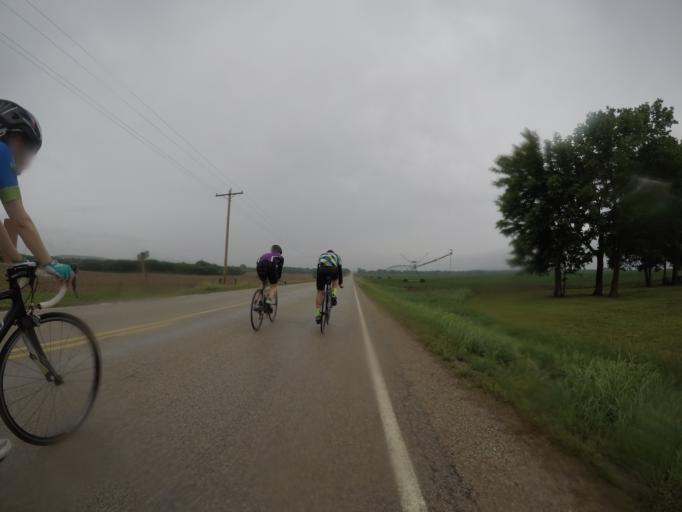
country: US
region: Kansas
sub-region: Pottawatomie County
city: Wamego
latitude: 39.3468
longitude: -96.2212
